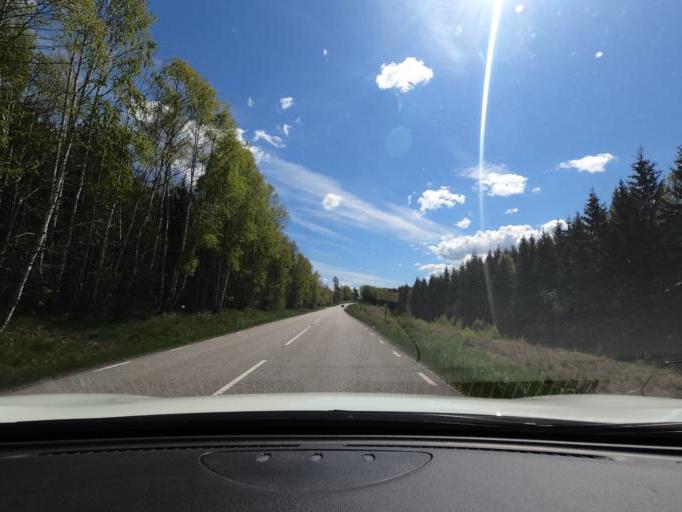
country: SE
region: Halland
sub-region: Kungsbacka Kommun
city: Fjaeras kyrkby
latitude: 57.4039
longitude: 12.2255
